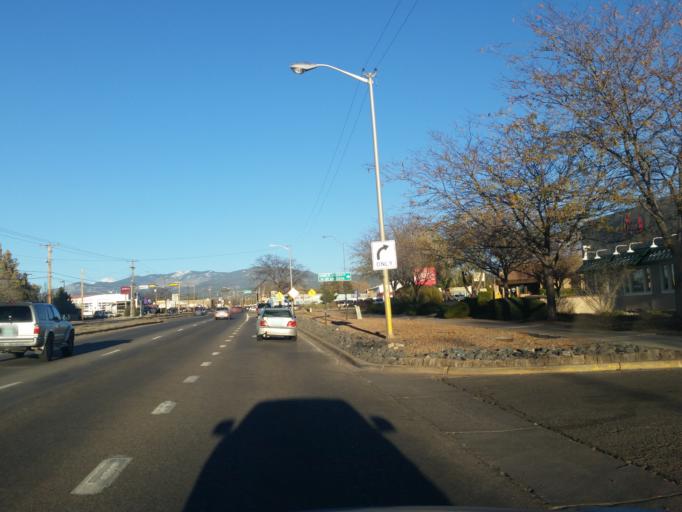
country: US
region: New Mexico
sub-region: Santa Fe County
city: Agua Fria
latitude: 35.6618
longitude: -105.9787
